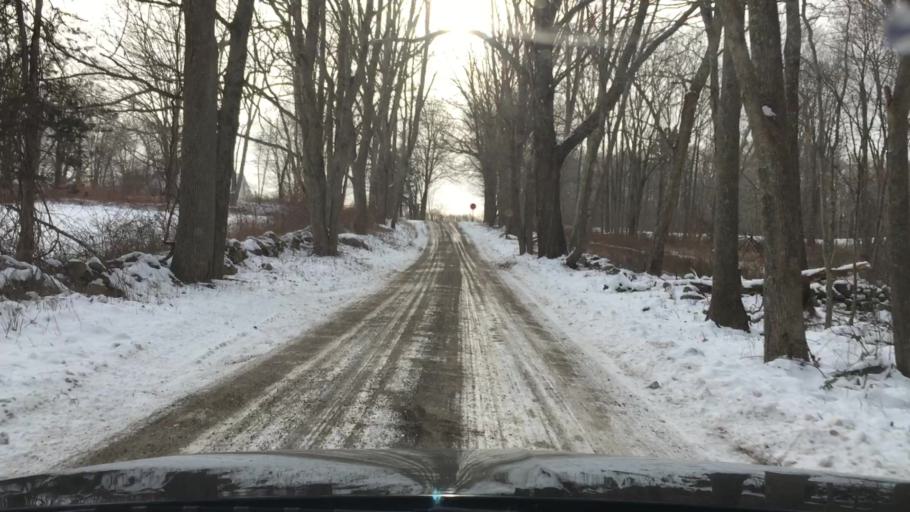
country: US
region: Connecticut
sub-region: Tolland County
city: Storrs
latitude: 41.8516
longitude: -72.1958
